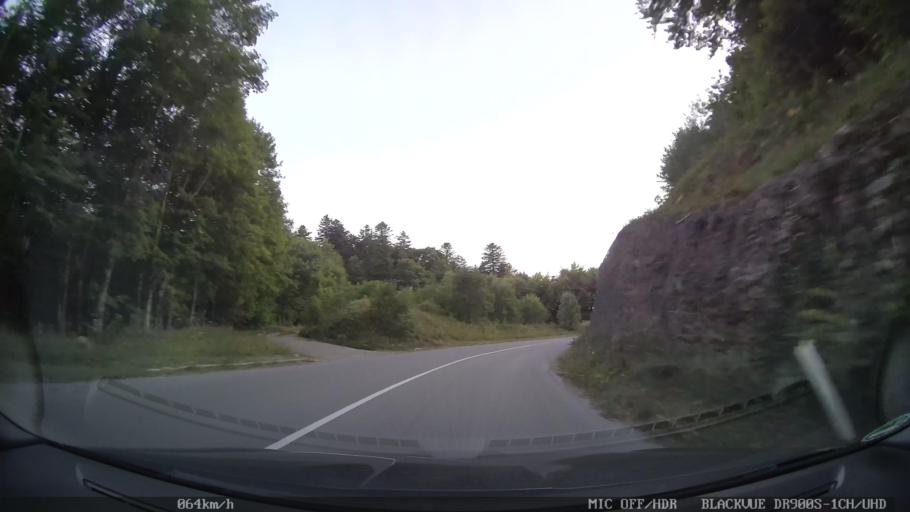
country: HR
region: Primorsko-Goranska
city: Novi Vinodolski
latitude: 45.1702
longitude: 14.9699
